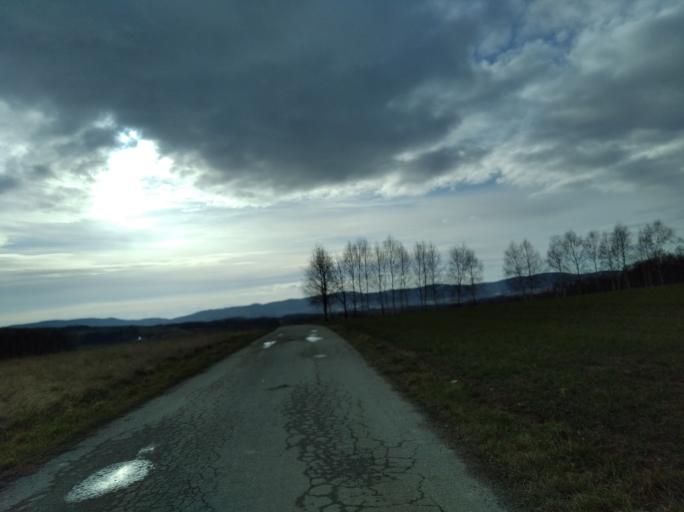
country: PL
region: Subcarpathian Voivodeship
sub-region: Powiat strzyzowski
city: Strzyzow
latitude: 49.8551
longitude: 21.7710
